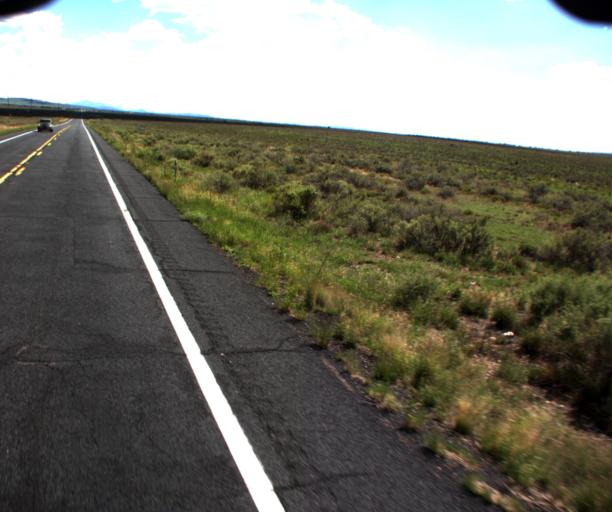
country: US
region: Arizona
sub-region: Coconino County
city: Williams
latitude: 35.6241
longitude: -112.1433
